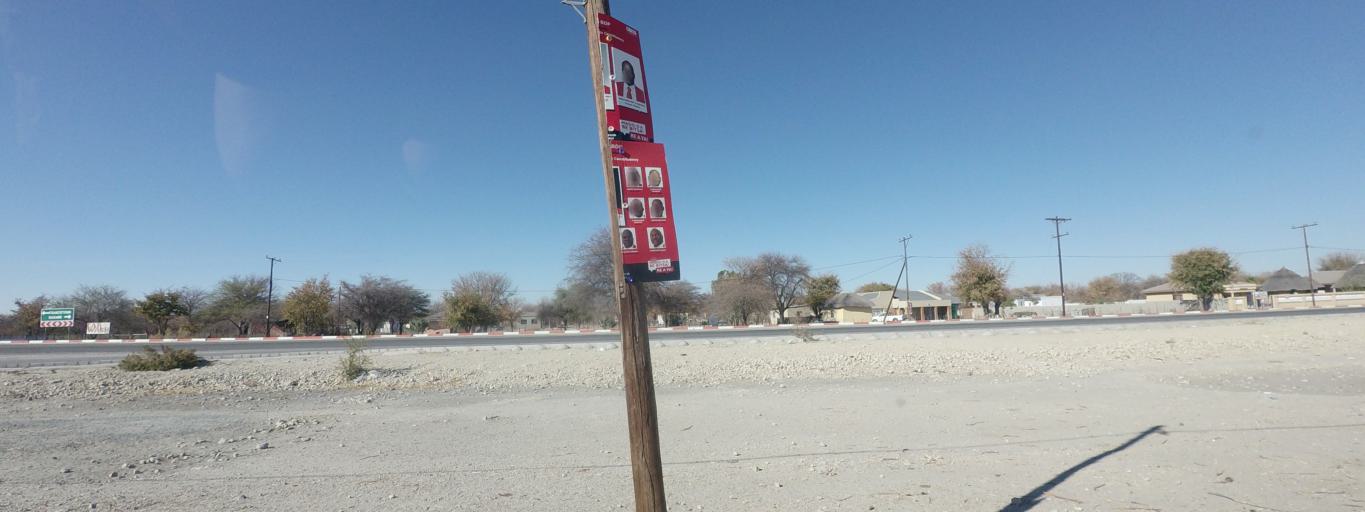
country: BW
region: Central
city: Nata
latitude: -20.2187
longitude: 26.1949
